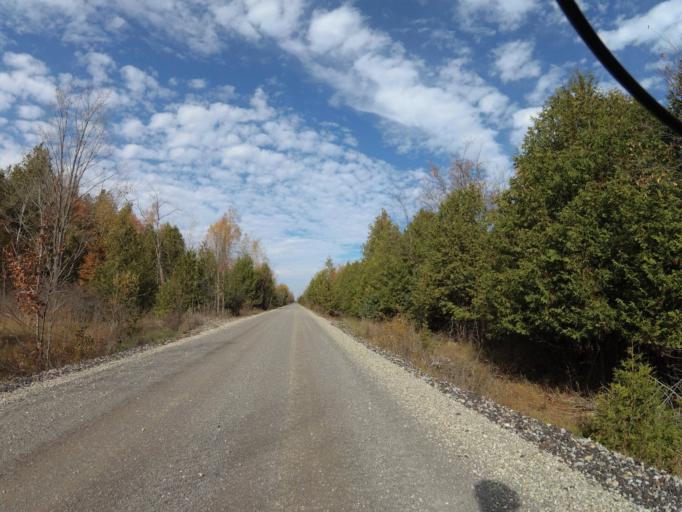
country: CA
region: Ontario
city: Carleton Place
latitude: 45.0672
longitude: -76.0970
